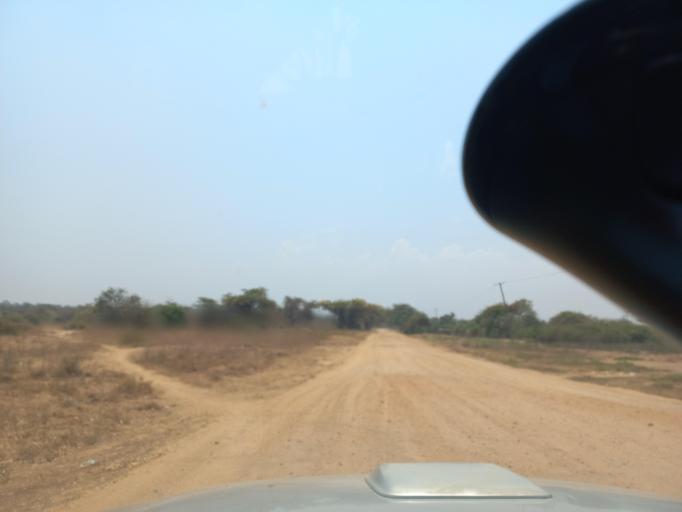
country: ZW
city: Chirundu
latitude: -15.9376
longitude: 28.8726
